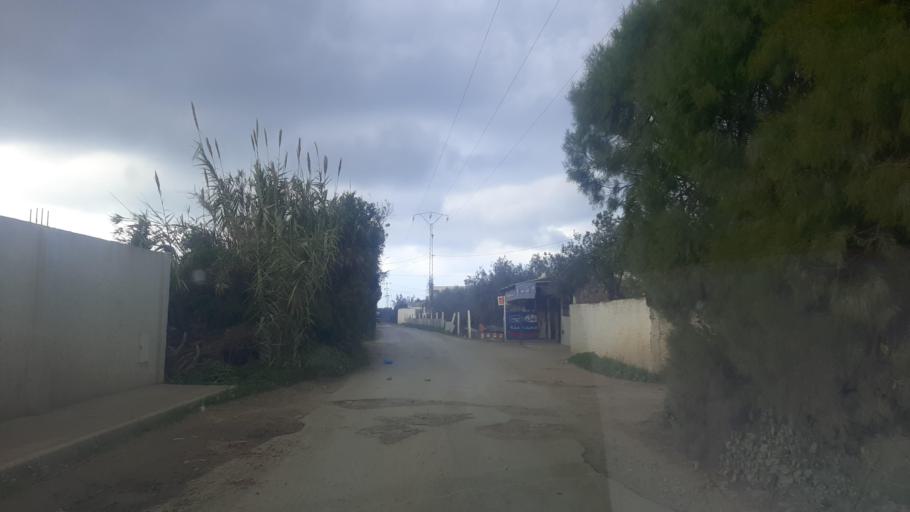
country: TN
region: Nabul
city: Manzil Bu Zalafah
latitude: 36.7344
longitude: 10.5353
